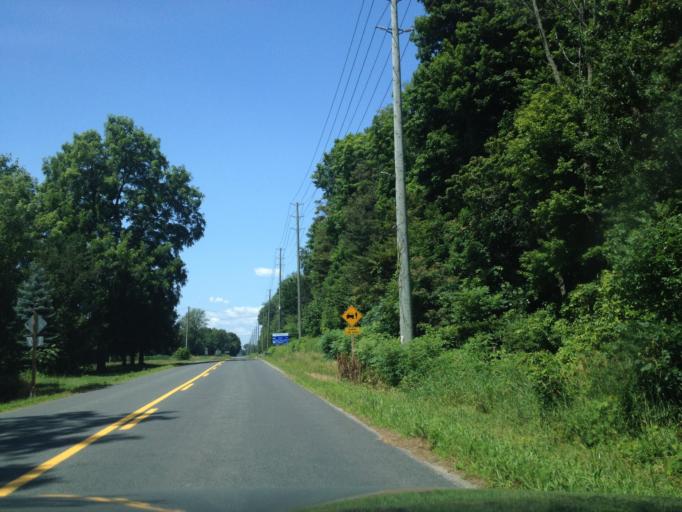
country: CA
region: Ontario
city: Aylmer
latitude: 42.6382
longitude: -80.7212
